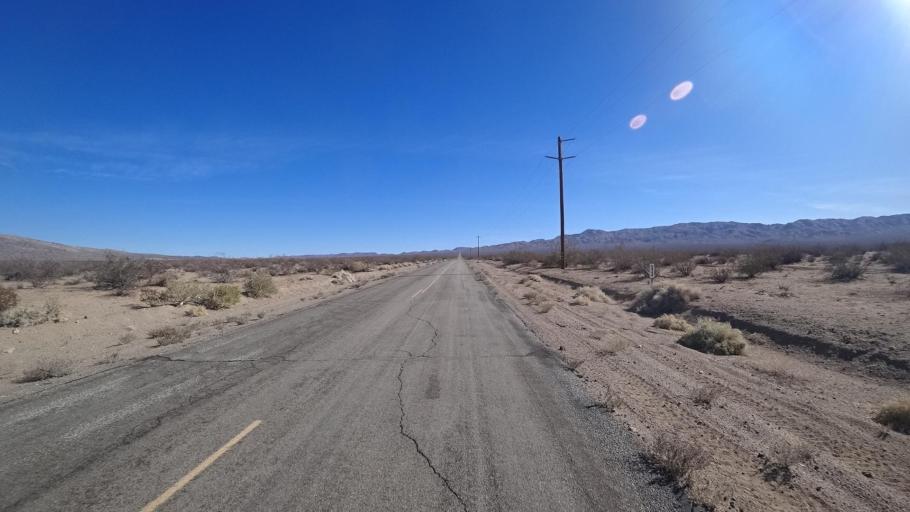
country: US
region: California
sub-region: Kern County
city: Ridgecrest
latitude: 35.3888
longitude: -117.7625
